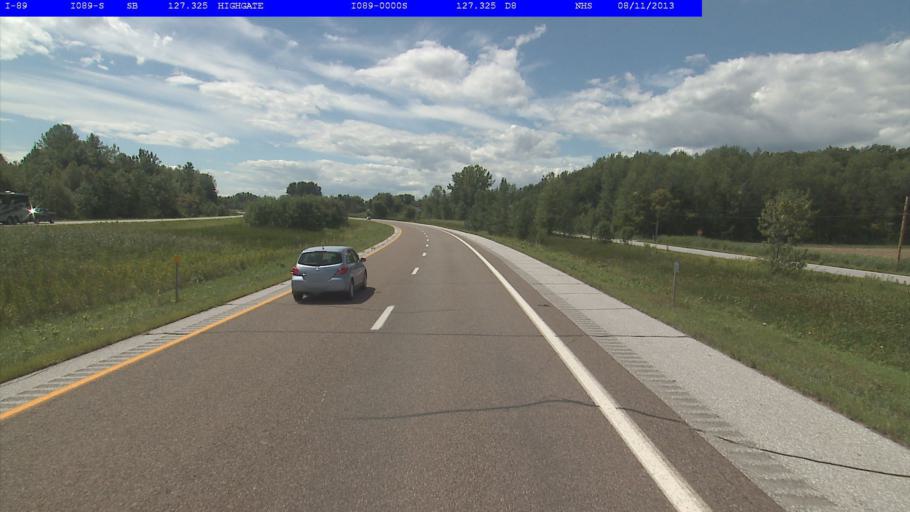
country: US
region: Vermont
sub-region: Franklin County
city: Swanton
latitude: 44.9773
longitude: -73.1012
